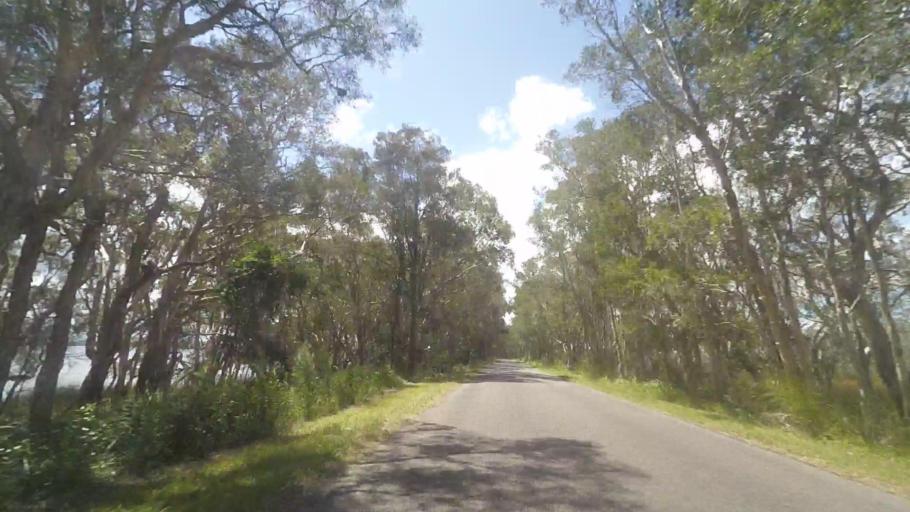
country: AU
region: New South Wales
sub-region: Great Lakes
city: Bulahdelah
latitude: -32.5203
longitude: 152.3225
